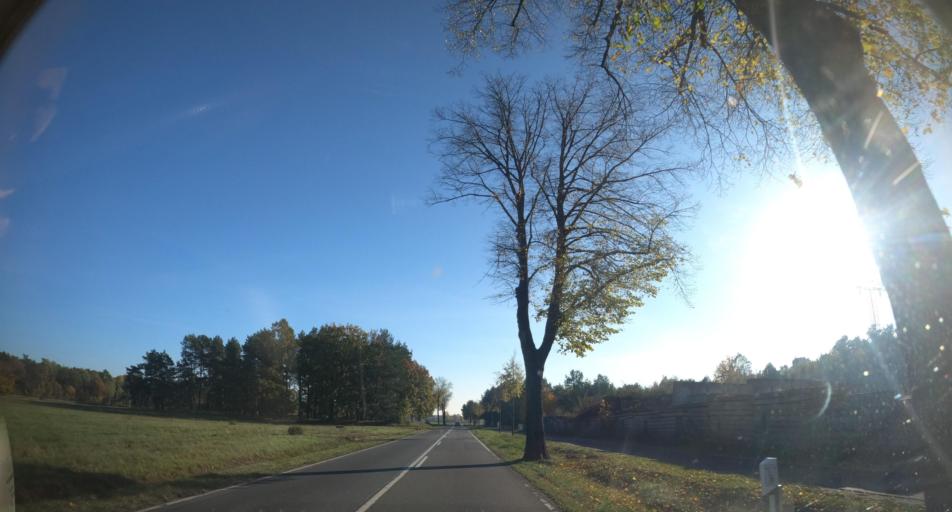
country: DE
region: Mecklenburg-Vorpommern
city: Ueckermunde
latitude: 53.7142
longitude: 14.0659
